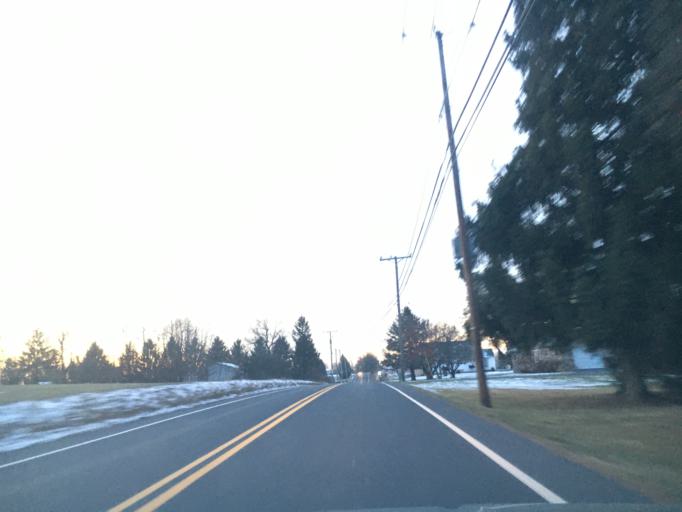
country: US
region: Pennsylvania
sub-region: Northampton County
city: Bath
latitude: 40.7809
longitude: -75.4084
